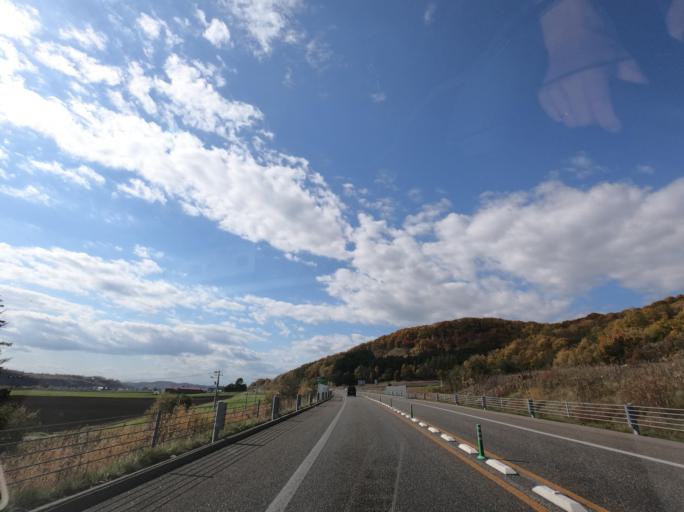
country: JP
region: Hokkaido
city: Otofuke
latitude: 43.1203
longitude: 143.6539
